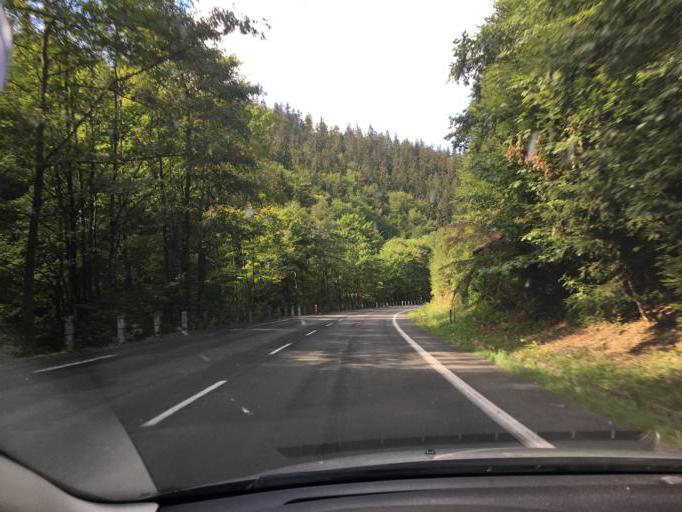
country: CZ
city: Benecko
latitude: 50.6744
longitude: 15.5931
